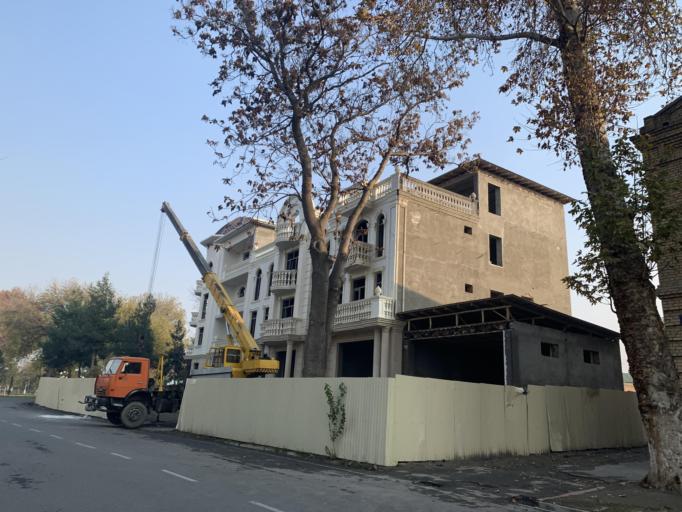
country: UZ
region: Fergana
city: Qo`qon
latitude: 40.5364
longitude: 70.9351
